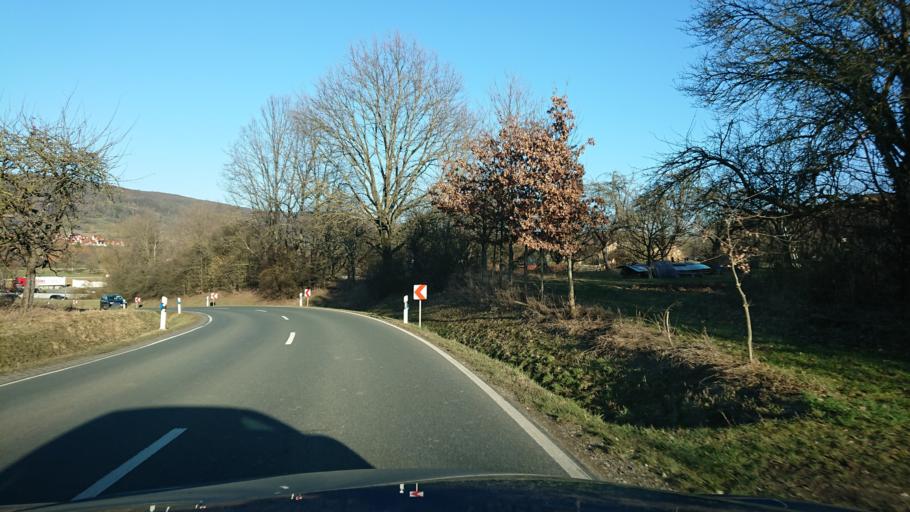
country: DE
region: Bavaria
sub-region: Upper Franconia
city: Pretzfeld
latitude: 49.7476
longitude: 11.1679
